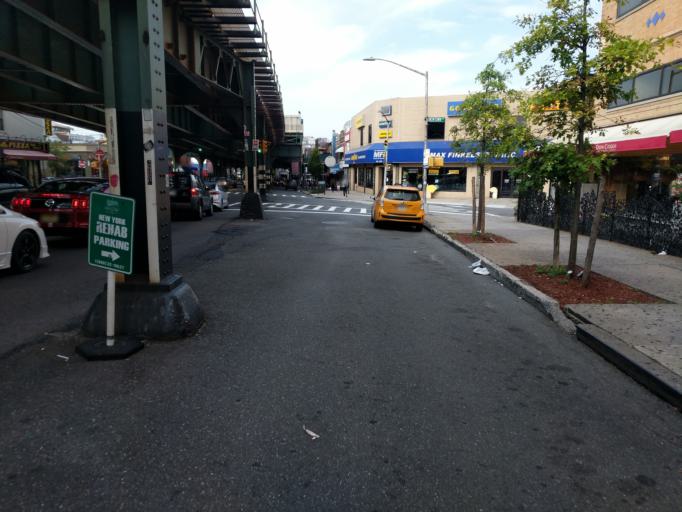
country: US
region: New York
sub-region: Queens County
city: Long Island City
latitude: 40.7681
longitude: -73.9205
